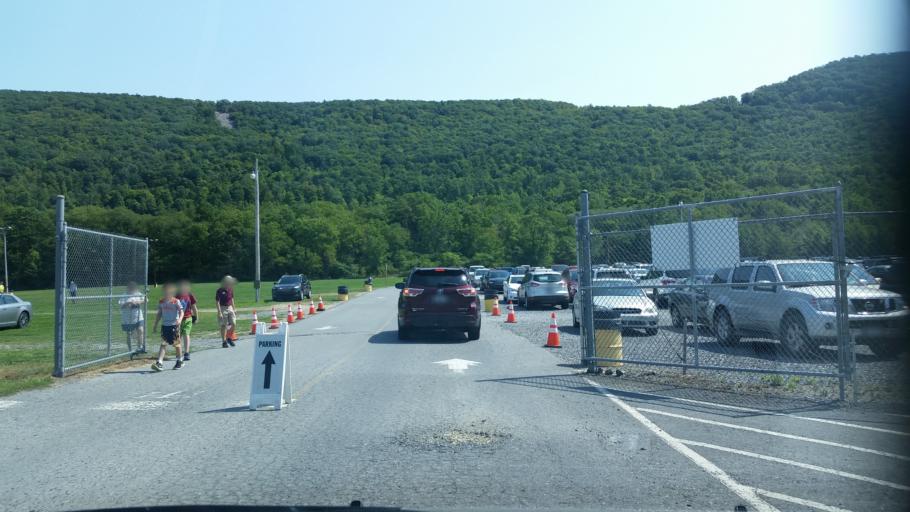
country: US
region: Pennsylvania
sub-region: Blair County
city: Tipton
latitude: 40.6305
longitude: -78.2887
